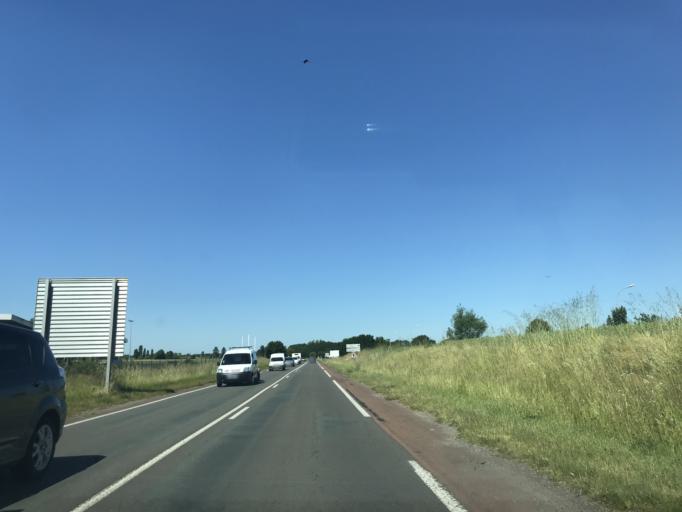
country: FR
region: Poitou-Charentes
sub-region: Departement de la Charente-Maritime
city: Gemozac
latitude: 45.5767
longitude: -0.6786
